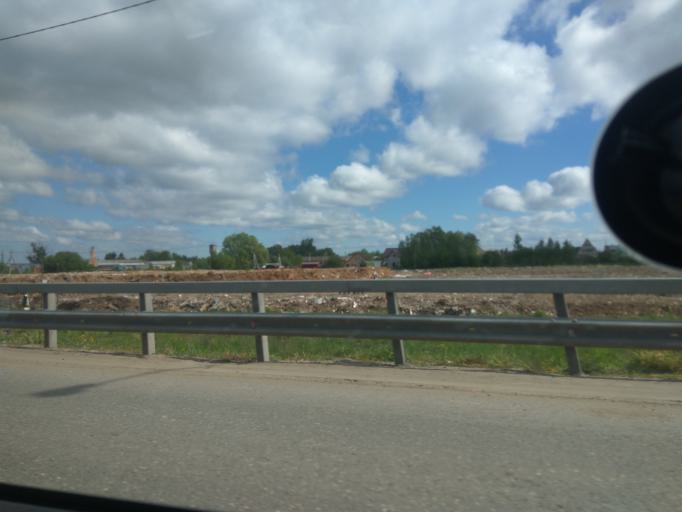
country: RU
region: Moskovskaya
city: Ostrovtsy
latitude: 55.5634
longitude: 38.0493
